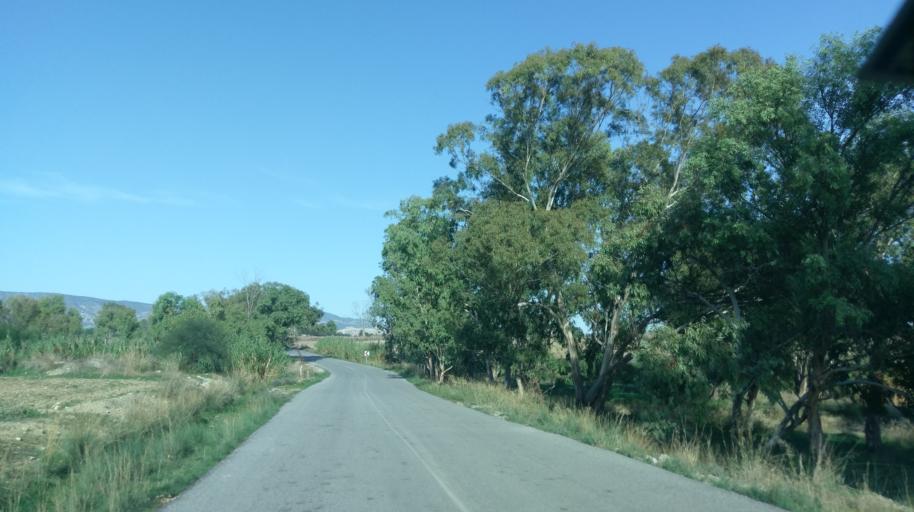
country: CY
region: Ammochostos
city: Lefkonoiko
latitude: 35.2928
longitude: 33.7373
